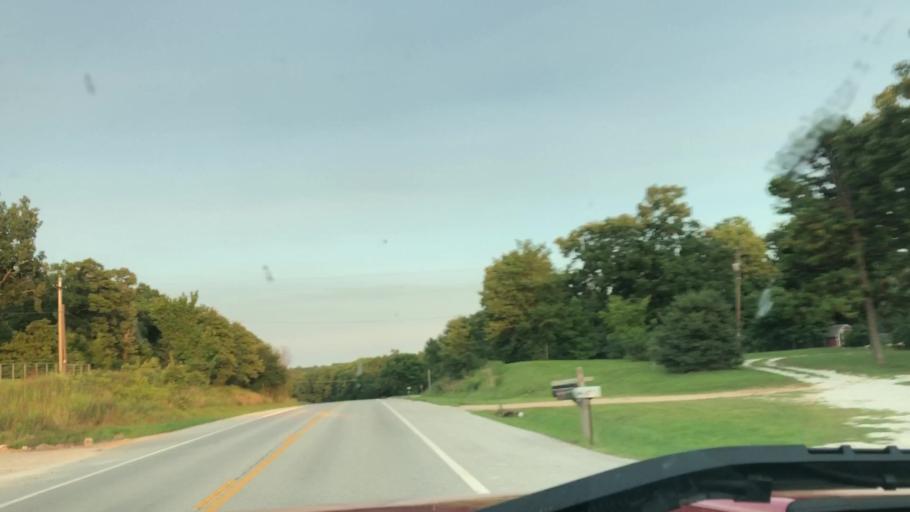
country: US
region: Missouri
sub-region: Jasper County
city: Duquesne
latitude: 36.9702
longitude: -94.4466
